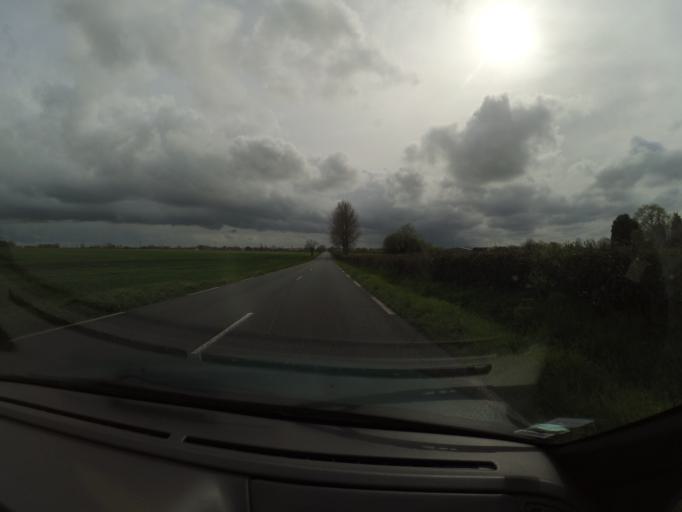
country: FR
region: Pays de la Loire
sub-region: Departement de Maine-et-Loire
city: Landemont
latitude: 47.2487
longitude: -1.2085
